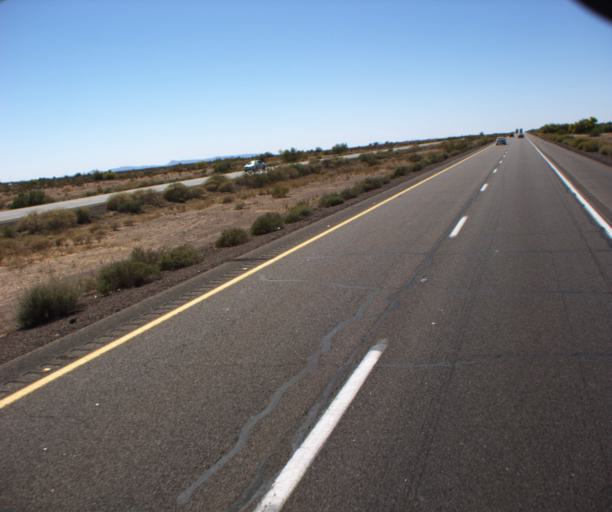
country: US
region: Arizona
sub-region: Maricopa County
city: Gila Bend
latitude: 32.8752
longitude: -113.1241
